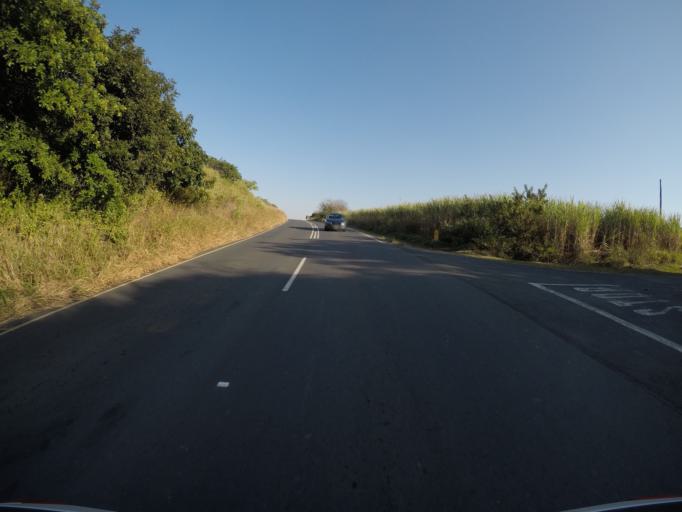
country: ZA
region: KwaZulu-Natal
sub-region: iLembe District Municipality
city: Stanger
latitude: -29.4271
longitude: 31.2710
